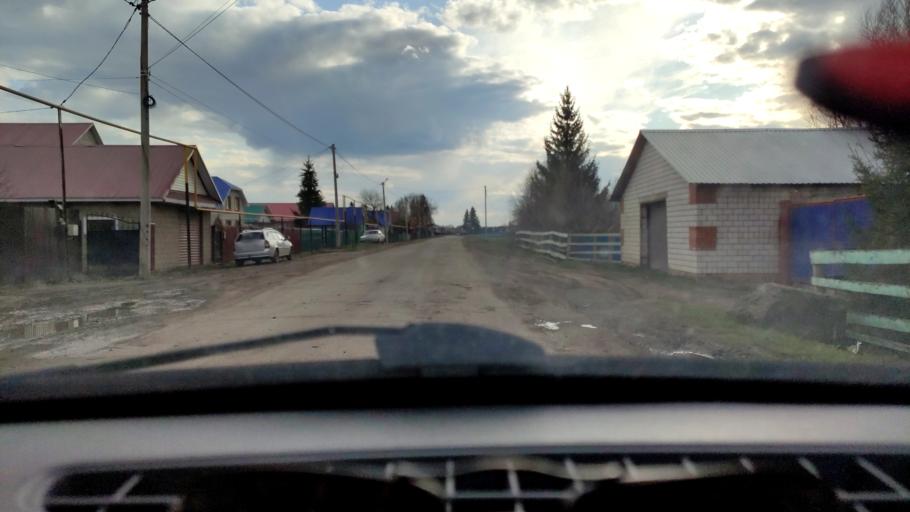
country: RU
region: Bashkortostan
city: Karmaskaly
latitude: 54.3721
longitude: 56.1973
